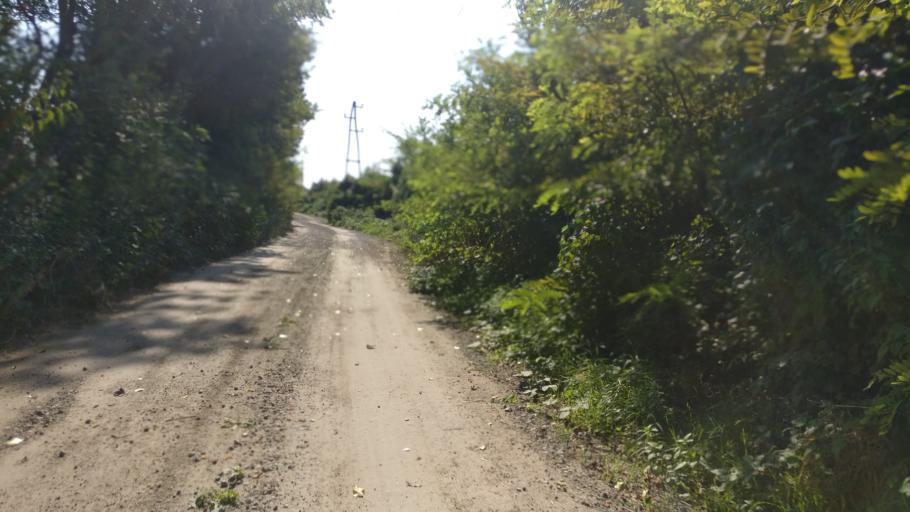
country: AT
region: Lower Austria
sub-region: Politischer Bezirk Baden
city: Ebreichsdorf
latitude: 47.9825
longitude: 16.4064
